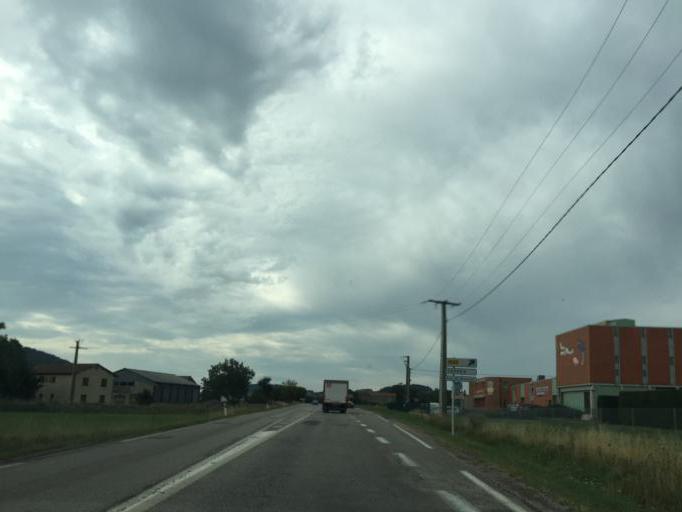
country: FR
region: Auvergne
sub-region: Departement de la Haute-Loire
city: Solignac-sur-Loire
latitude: 44.9645
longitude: 3.8445
